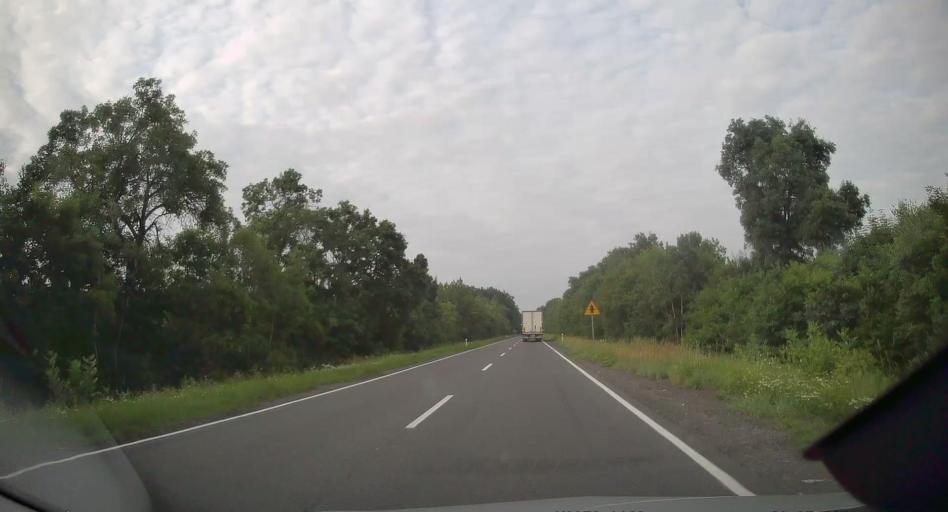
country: PL
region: Silesian Voivodeship
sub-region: Powiat czestochowski
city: Klomnice
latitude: 50.9463
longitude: 19.3943
